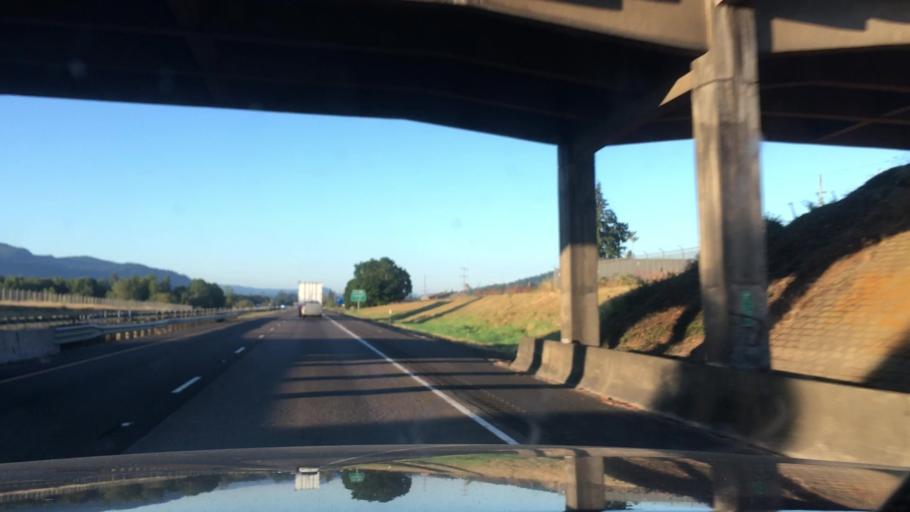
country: US
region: Oregon
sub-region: Lane County
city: Creswell
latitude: 43.9380
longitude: -123.0097
